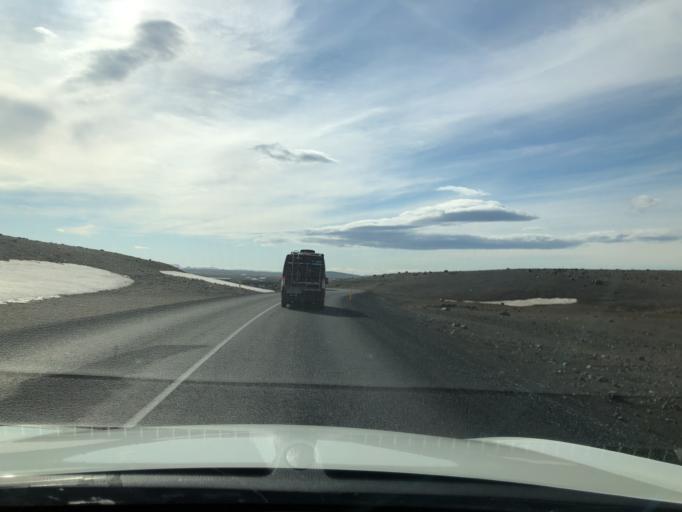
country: IS
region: Northeast
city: Husavik
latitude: 65.8122
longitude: -16.4071
